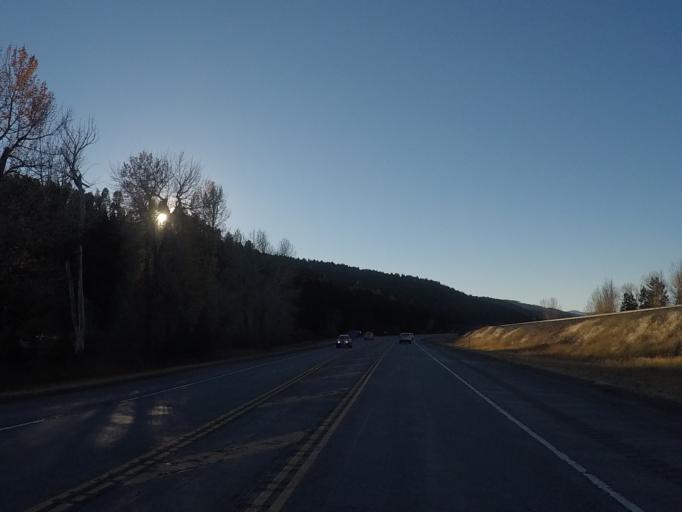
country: US
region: Montana
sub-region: Lewis and Clark County
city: Helena West Side
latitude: 46.5567
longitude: -112.4105
